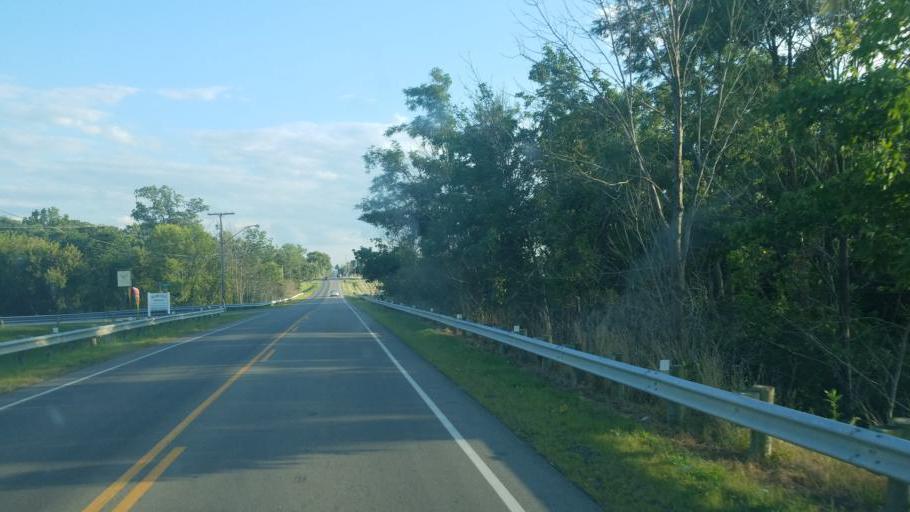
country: US
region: Ohio
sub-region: Huron County
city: Willard
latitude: 41.0571
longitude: -82.7163
